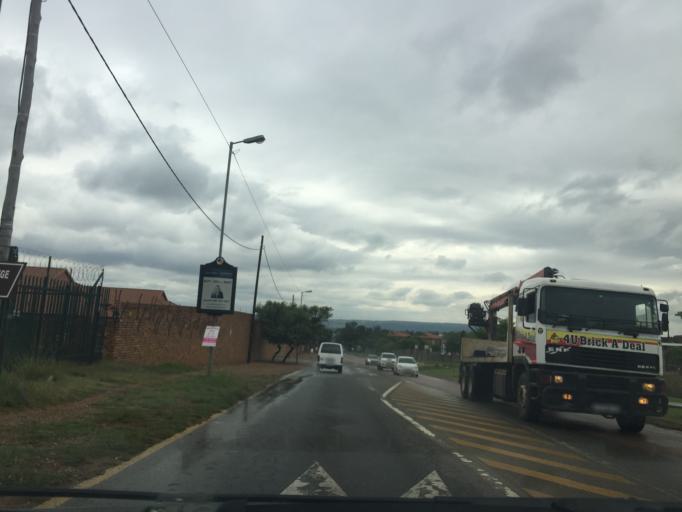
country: ZA
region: Gauteng
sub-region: City of Tshwane Metropolitan Municipality
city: Pretoria
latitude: -25.7828
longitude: 28.3600
